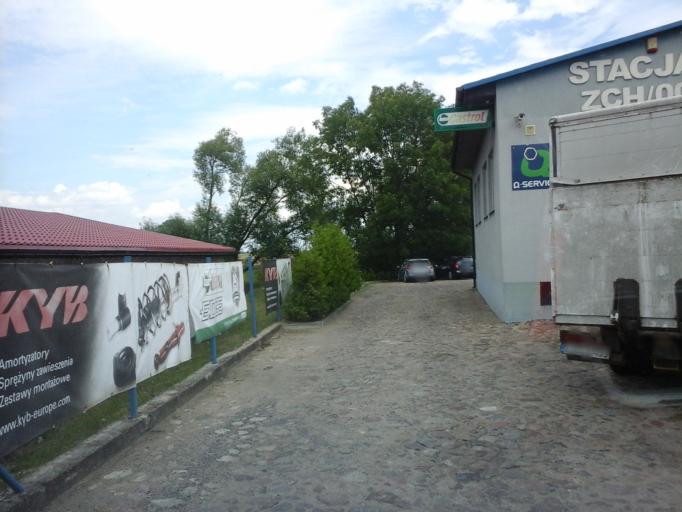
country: PL
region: West Pomeranian Voivodeship
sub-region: Powiat choszczenski
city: Bierzwnik
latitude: 53.0366
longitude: 15.6653
